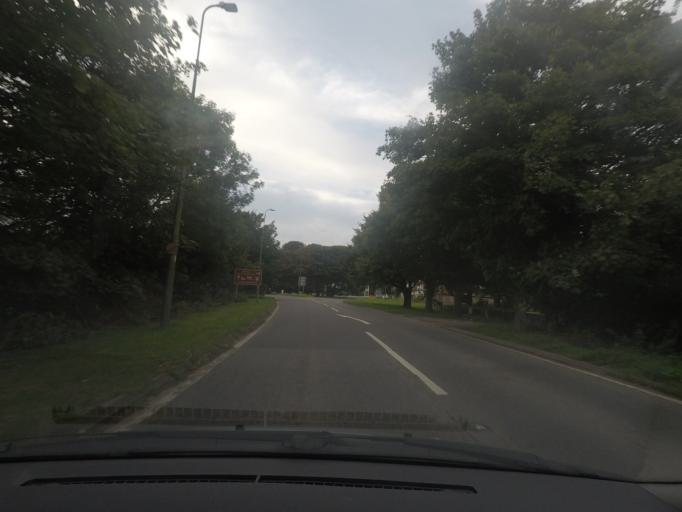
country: GB
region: England
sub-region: Lincolnshire
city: Alford
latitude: 53.2406
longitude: 0.1155
